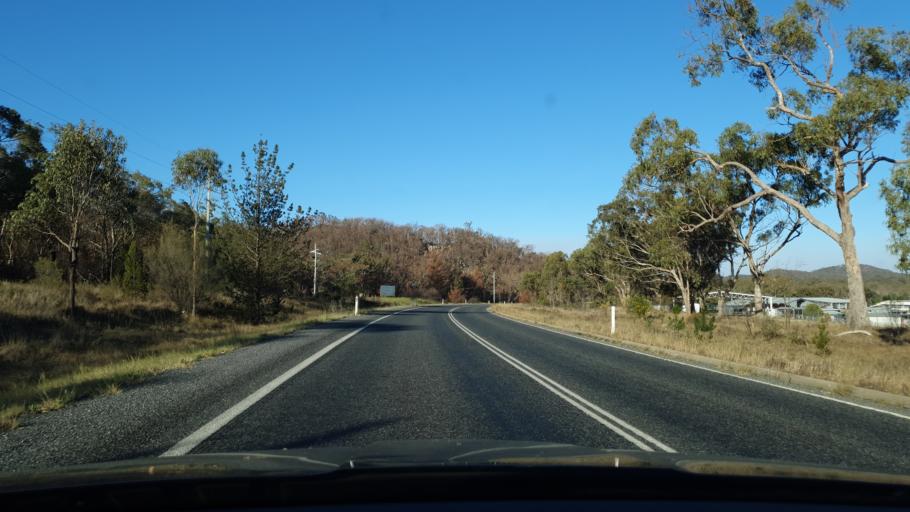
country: AU
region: Queensland
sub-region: Southern Downs
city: Stanthorpe
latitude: -28.6458
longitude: 151.9263
